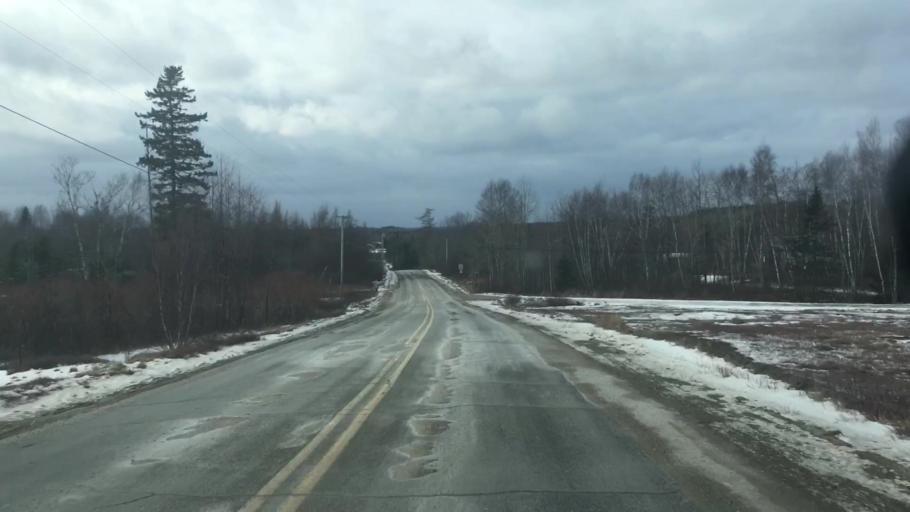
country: US
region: Maine
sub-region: Washington County
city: Machias
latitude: 44.6558
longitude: -67.5217
